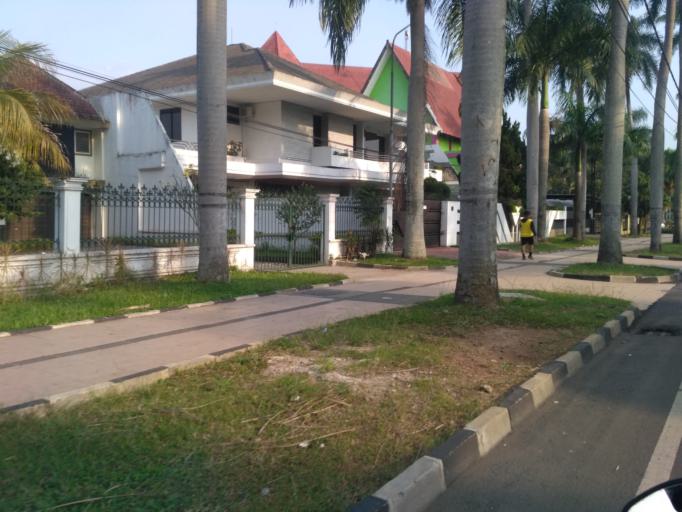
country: ID
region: East Java
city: Malang
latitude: -7.9714
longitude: 112.6222
